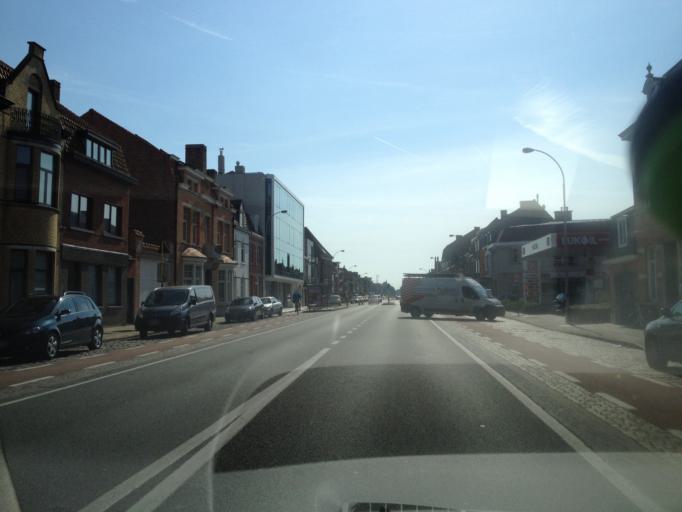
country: BE
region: Flanders
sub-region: Provincie West-Vlaanderen
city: Brugge
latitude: 51.2015
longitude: 3.2014
